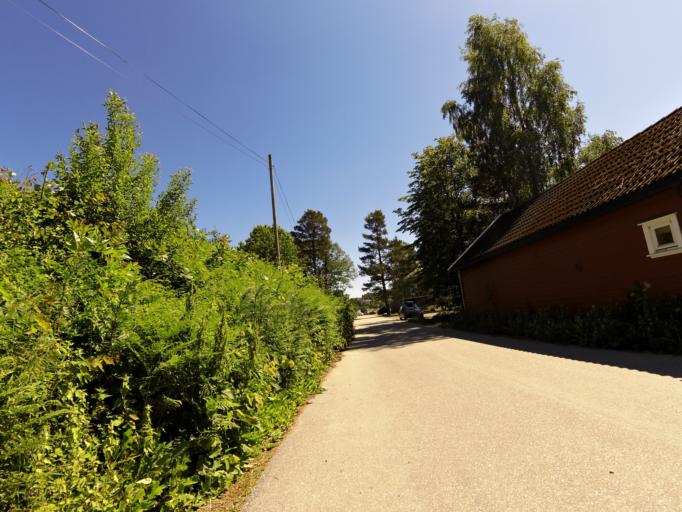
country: NO
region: Vest-Agder
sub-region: Kristiansand
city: Justvik
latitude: 58.1922
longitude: 8.0798
